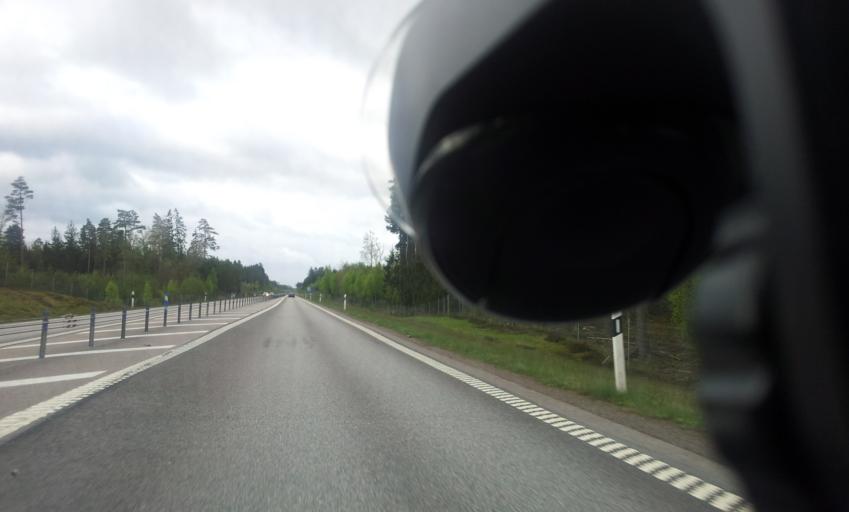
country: SE
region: Kalmar
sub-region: Kalmar Kommun
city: Ljungbyholm
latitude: 56.5290
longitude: 16.0843
